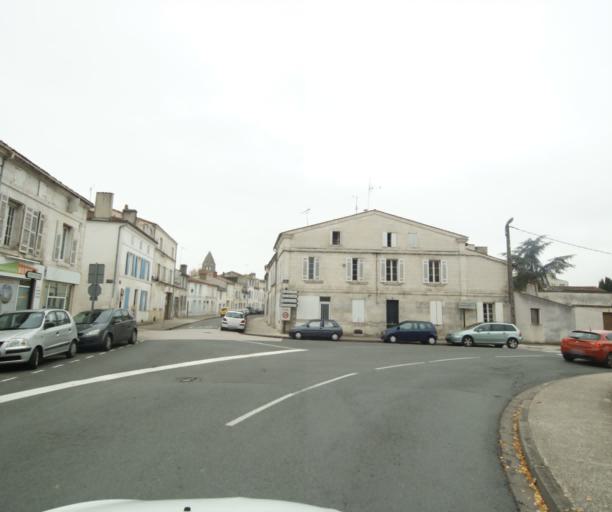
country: FR
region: Poitou-Charentes
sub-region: Departement de la Charente-Maritime
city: Saintes
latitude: 45.7451
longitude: -0.6211
